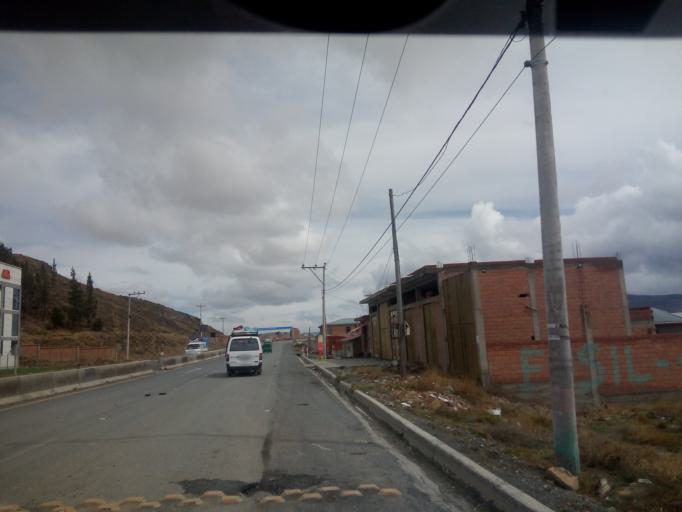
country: BO
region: La Paz
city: Achacachi
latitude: -16.0555
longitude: -68.6802
